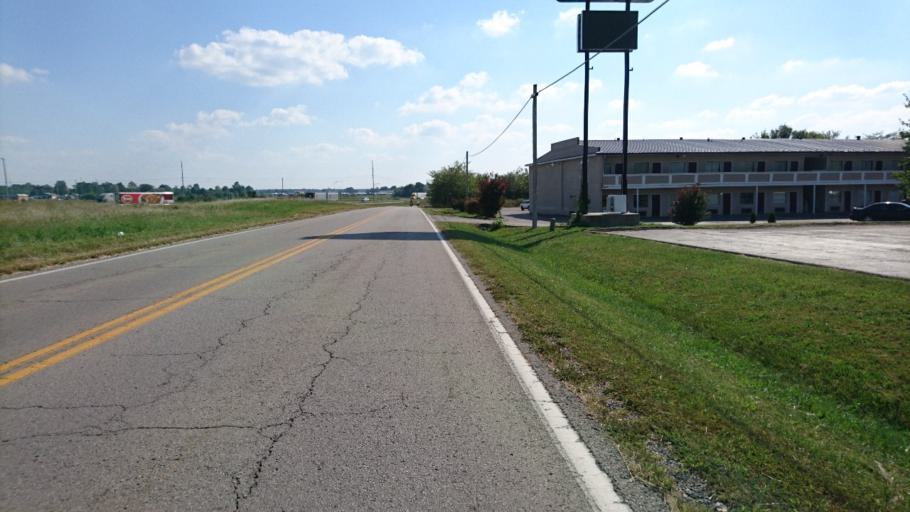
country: US
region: Missouri
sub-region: Laclede County
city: Lebanon
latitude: 37.6475
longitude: -92.6700
